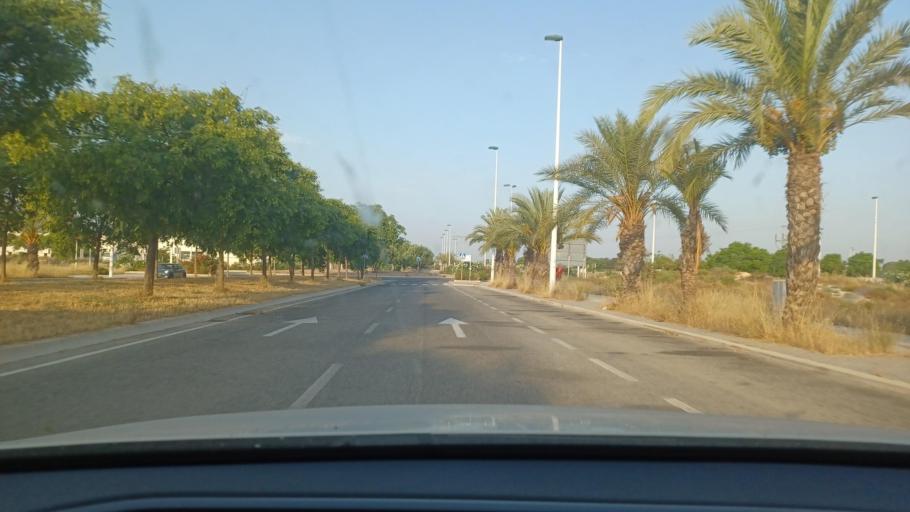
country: ES
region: Valencia
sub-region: Provincia de Alicante
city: Elche
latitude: 38.2871
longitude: -0.6230
